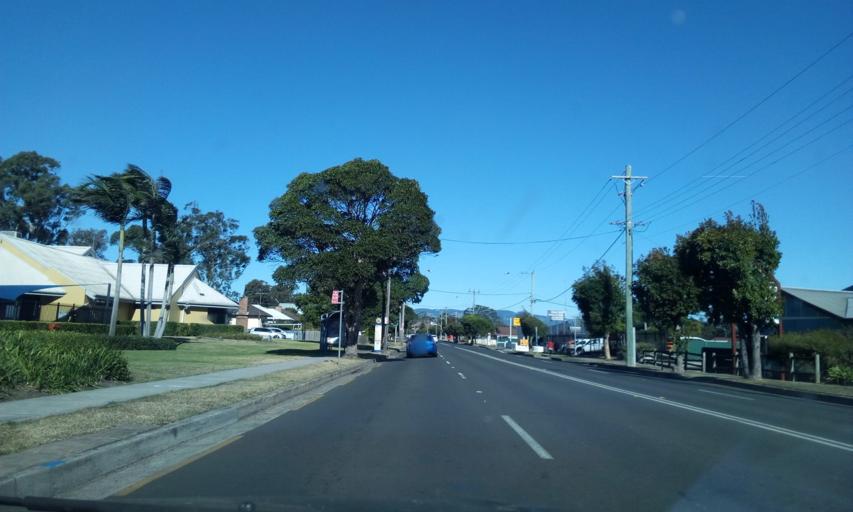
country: AU
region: New South Wales
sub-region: Wollongong
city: Dapto
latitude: -34.4964
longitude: 150.7926
